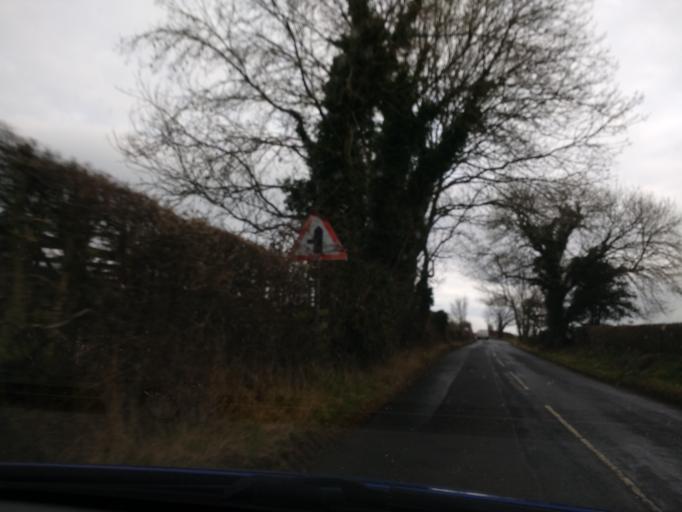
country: GB
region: England
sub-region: Lancashire
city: Caton
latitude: 54.0846
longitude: -2.7473
